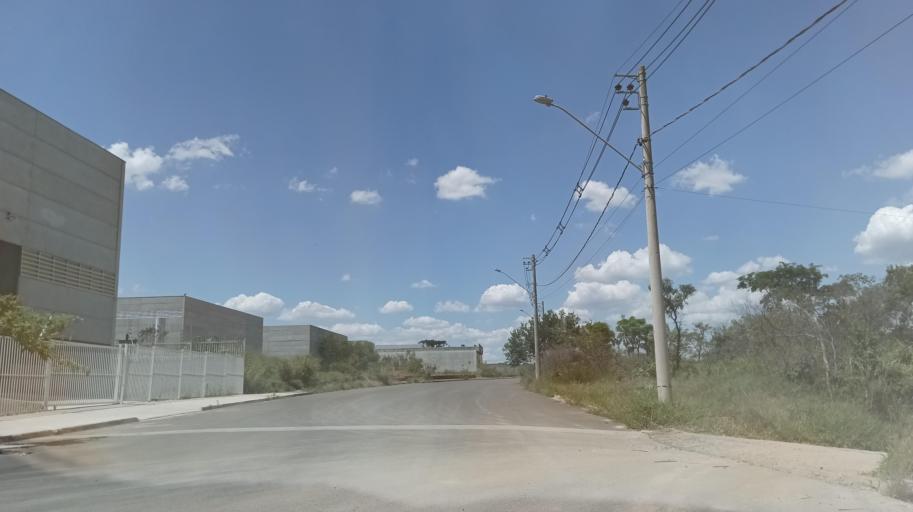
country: BR
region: Sao Paulo
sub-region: Sorocaba
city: Sorocaba
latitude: -23.4687
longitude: -47.4566
